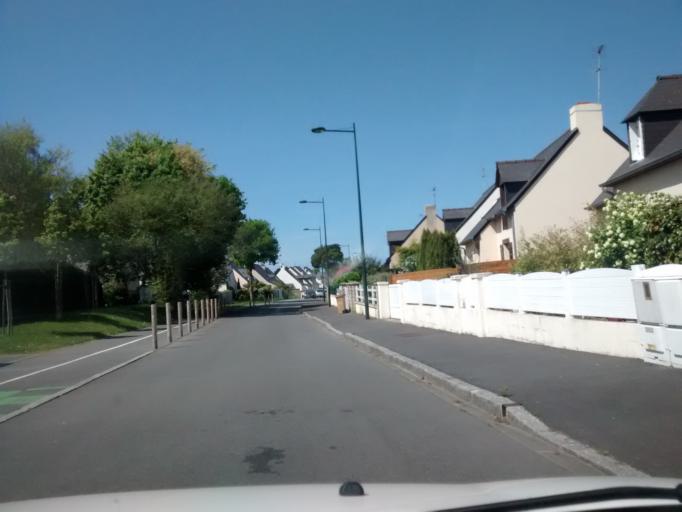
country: FR
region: Brittany
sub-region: Departement d'Ille-et-Vilaine
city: Dinard
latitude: 48.6245
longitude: -2.0726
